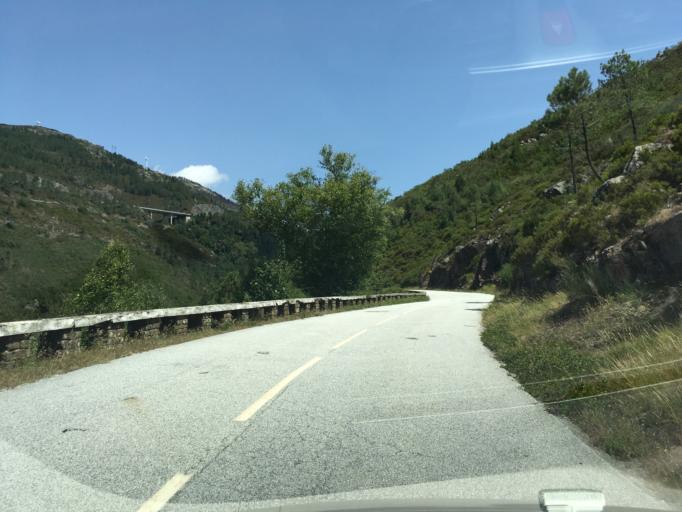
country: PT
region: Vila Real
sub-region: Mesao Frio
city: Mesao Frio
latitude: 41.2719
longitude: -7.9311
